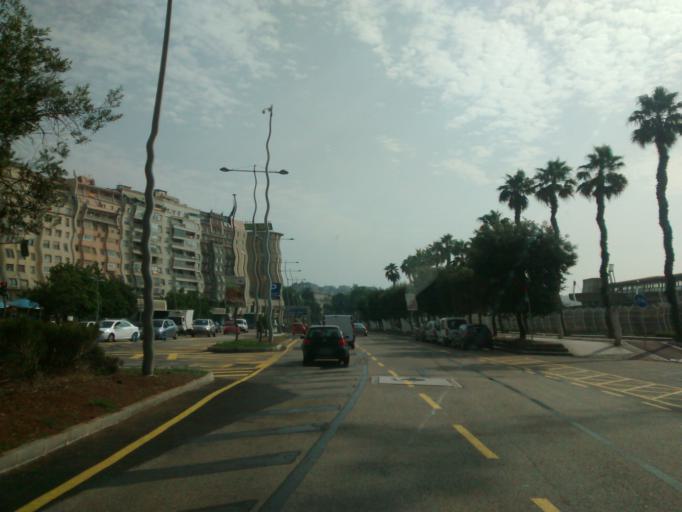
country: ES
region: Cantabria
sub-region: Provincia de Cantabria
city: Santander
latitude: 43.4583
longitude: -3.8083
